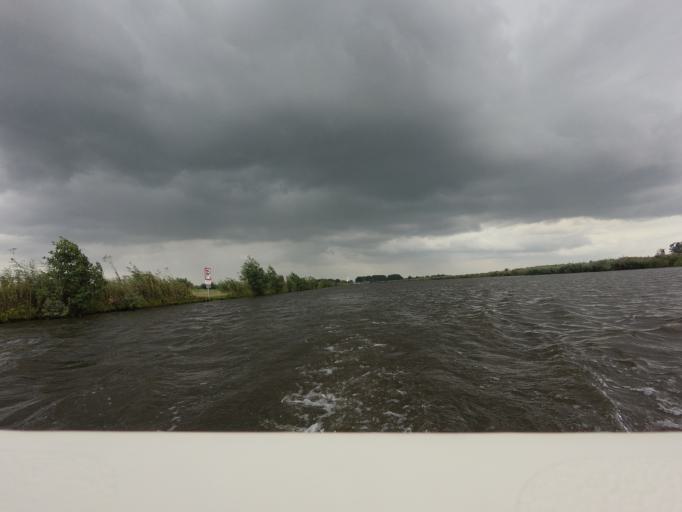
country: NL
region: Friesland
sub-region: Gemeente Smallingerland
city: Oudega
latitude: 53.1136
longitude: 5.9469
